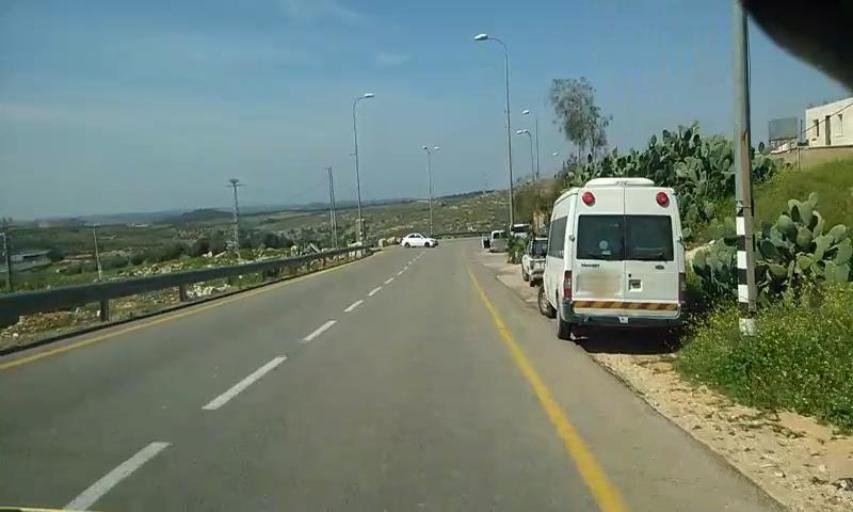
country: PS
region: West Bank
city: Surif
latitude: 31.6693
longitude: 35.0746
